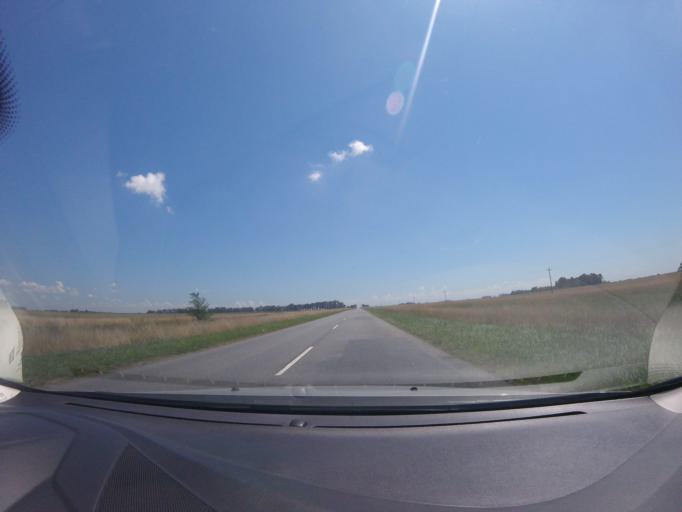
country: AR
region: Buenos Aires
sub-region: Partido de Rauch
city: Rauch
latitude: -36.5923
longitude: -59.0562
